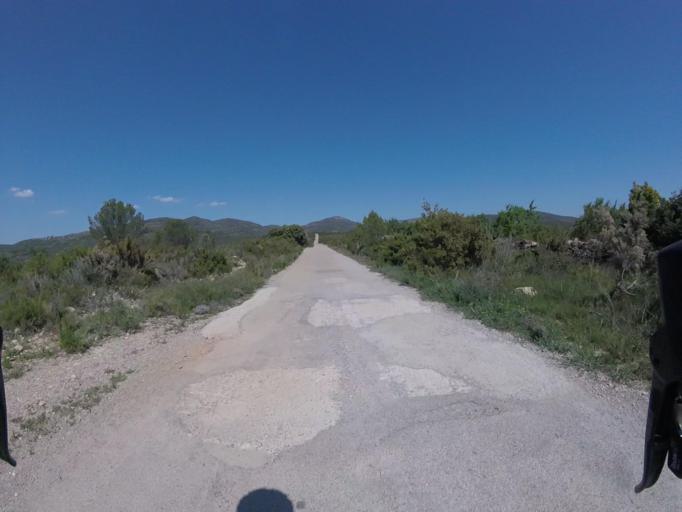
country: ES
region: Valencia
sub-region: Provincia de Castello
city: Sierra-Engarceran
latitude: 40.2288
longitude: -0.0238
